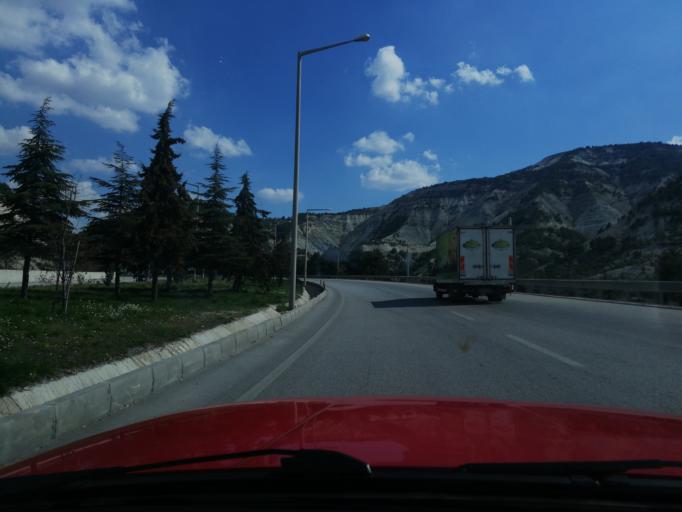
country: TR
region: Burdur
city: Burdur
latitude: 37.7101
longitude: 30.2950
